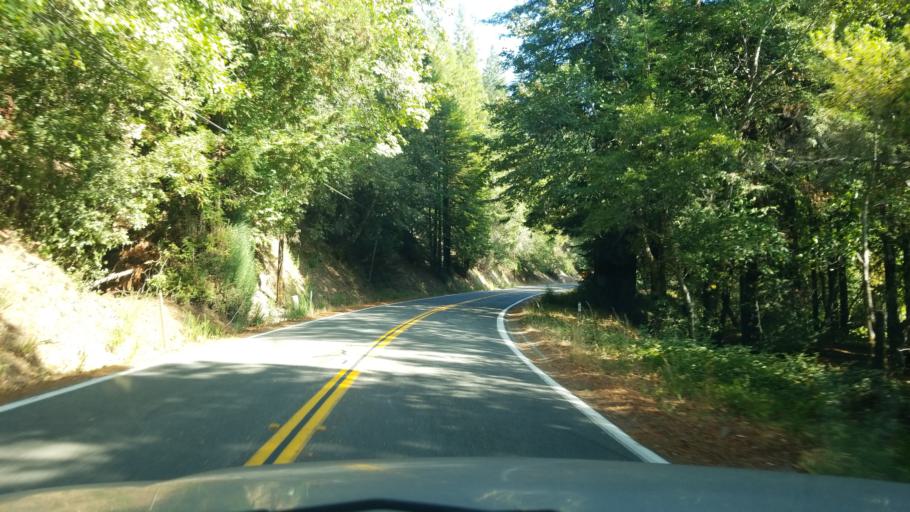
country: US
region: California
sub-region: Humboldt County
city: Redway
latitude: 40.2219
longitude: -123.7881
